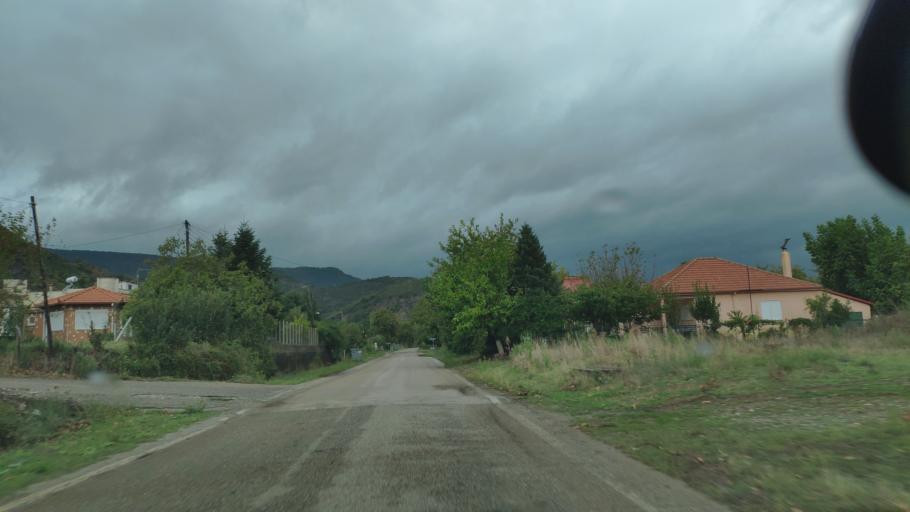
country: GR
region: West Greece
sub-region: Nomos Aitolias kai Akarnanias
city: Krikellos
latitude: 38.9865
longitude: 21.3196
